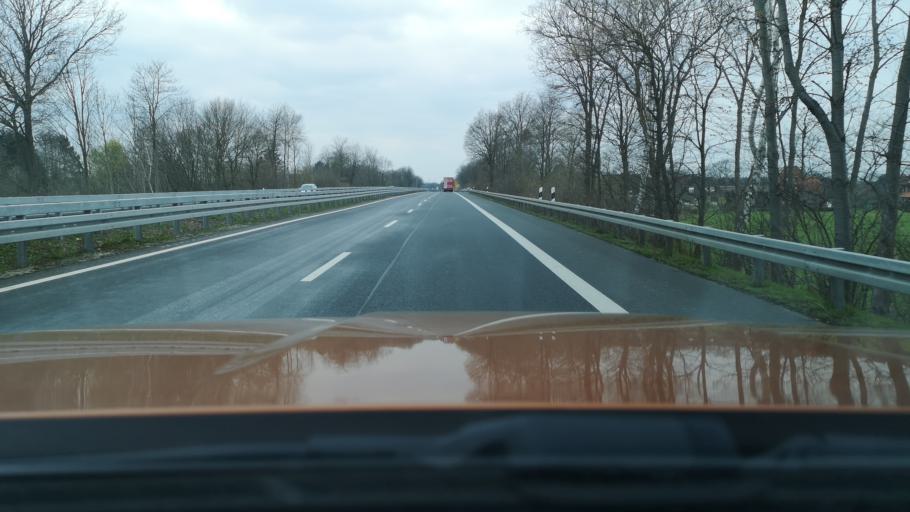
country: DE
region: Lower Saxony
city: Stadthagen
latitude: 52.3108
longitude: 9.2077
